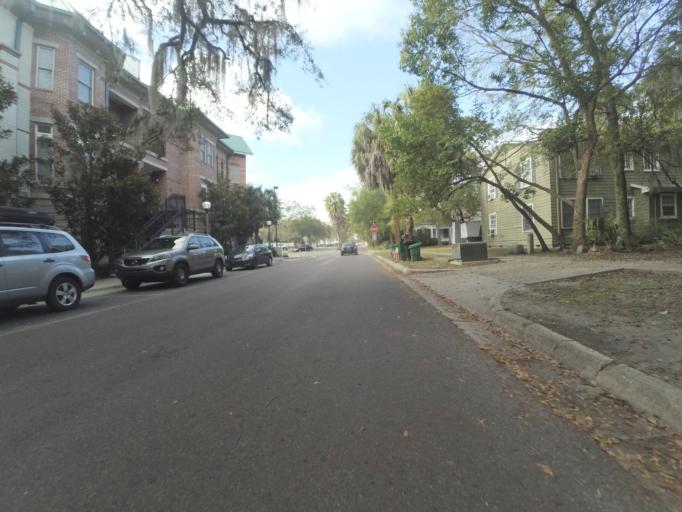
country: US
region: Florida
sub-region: Alachua County
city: Gainesville
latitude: 29.6531
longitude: -82.3218
